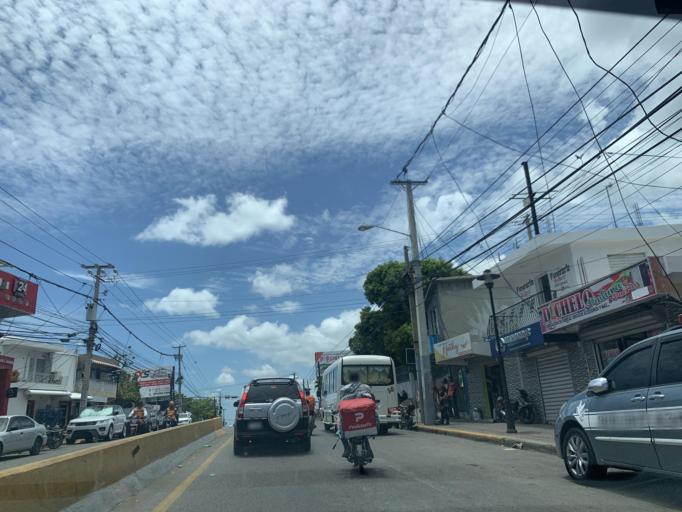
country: DO
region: Puerto Plata
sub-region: Puerto Plata
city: Puerto Plata
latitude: 19.7863
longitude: -70.6891
